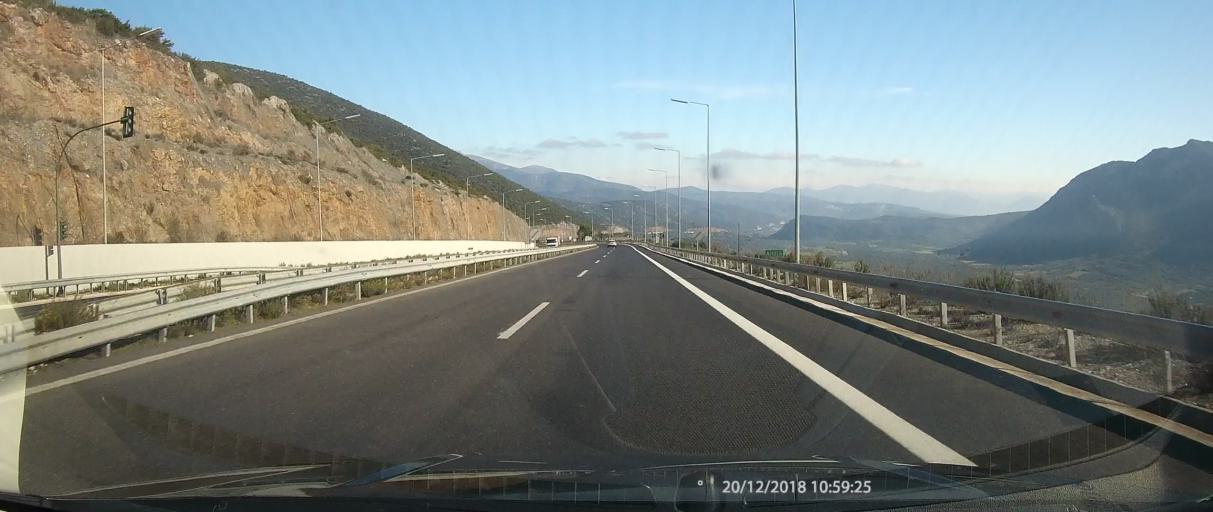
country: GR
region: Peloponnese
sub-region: Nomos Korinthias
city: Nemea
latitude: 37.6973
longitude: 22.5308
